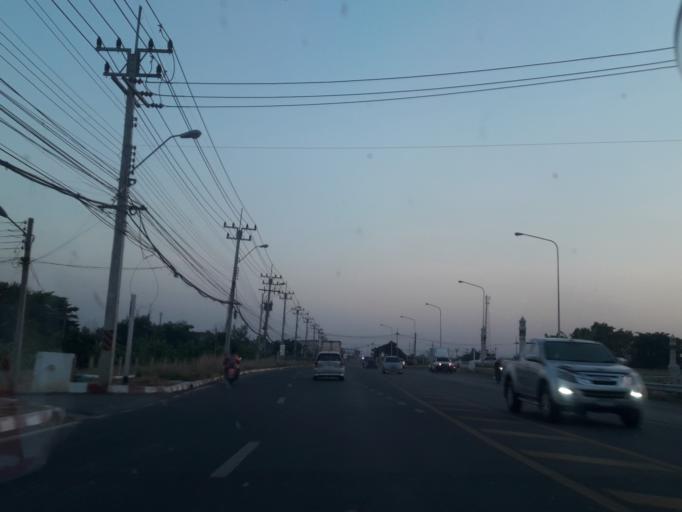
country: TH
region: Pathum Thani
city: Thanyaburi
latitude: 14.0724
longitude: 100.7102
